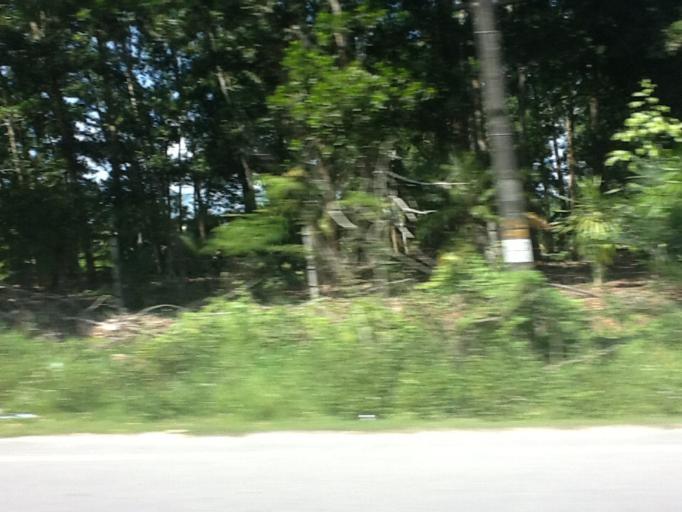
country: TH
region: Phuket
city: Thalang
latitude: 8.0887
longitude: 98.3457
